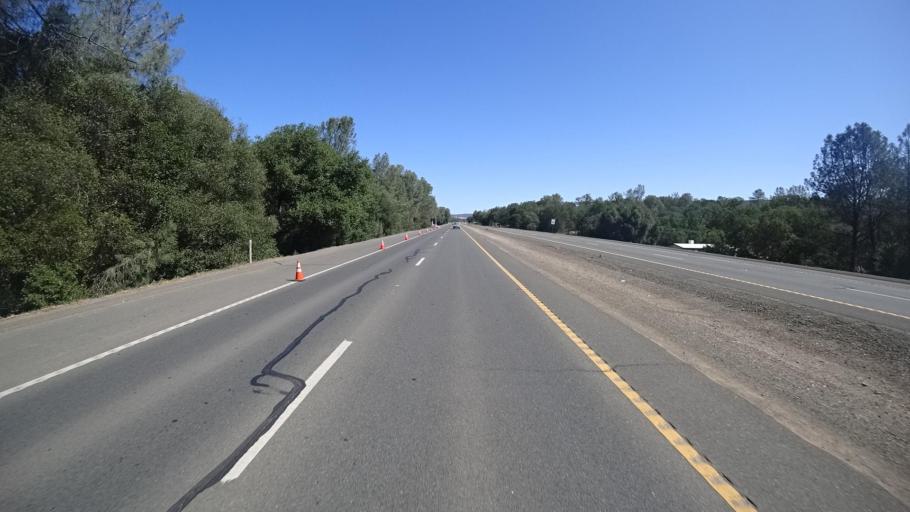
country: US
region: California
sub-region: Lake County
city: Clearlake
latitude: 38.9428
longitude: -122.6235
